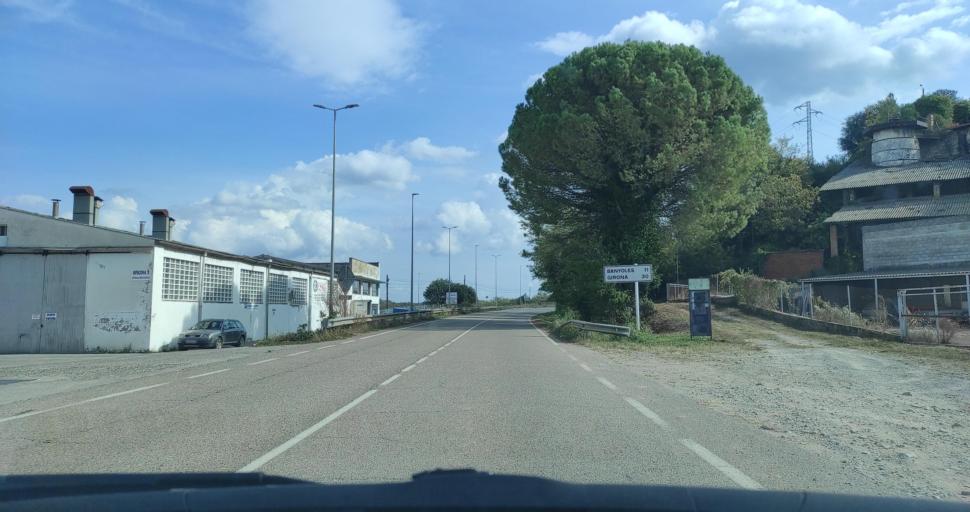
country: ES
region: Catalonia
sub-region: Provincia de Girona
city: Besalu
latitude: 42.1985
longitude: 2.7057
